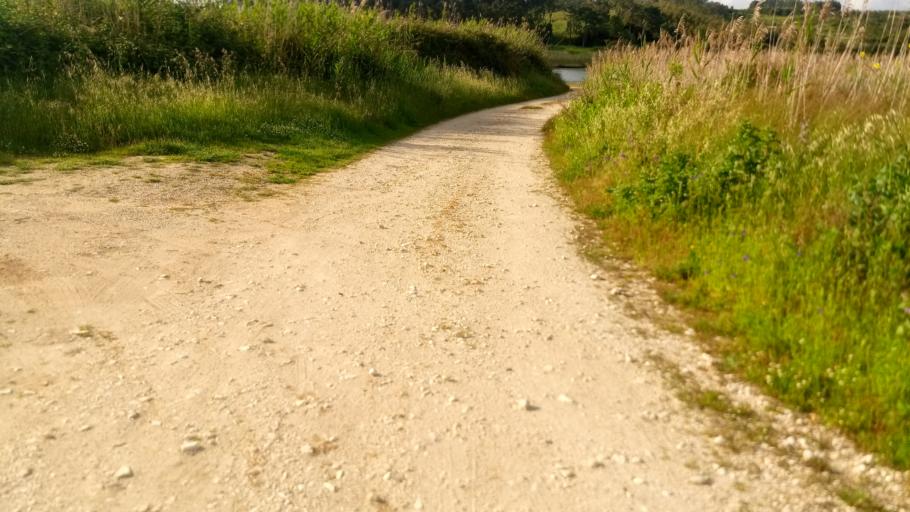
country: PT
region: Leiria
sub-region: Caldas da Rainha
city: Caldas da Rainha
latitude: 39.4030
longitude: -9.1944
